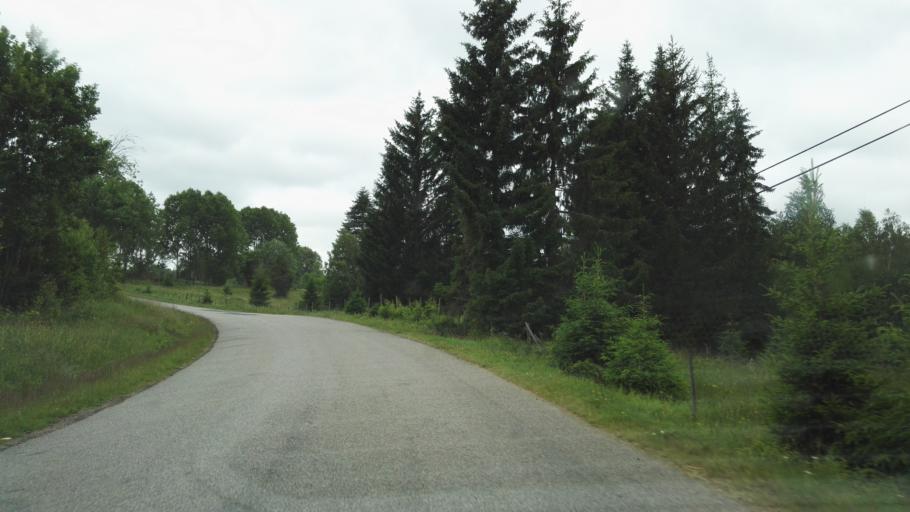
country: SE
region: Joenkoeping
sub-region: Vetlanda Kommun
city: Landsbro
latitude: 57.2916
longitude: 14.8366
